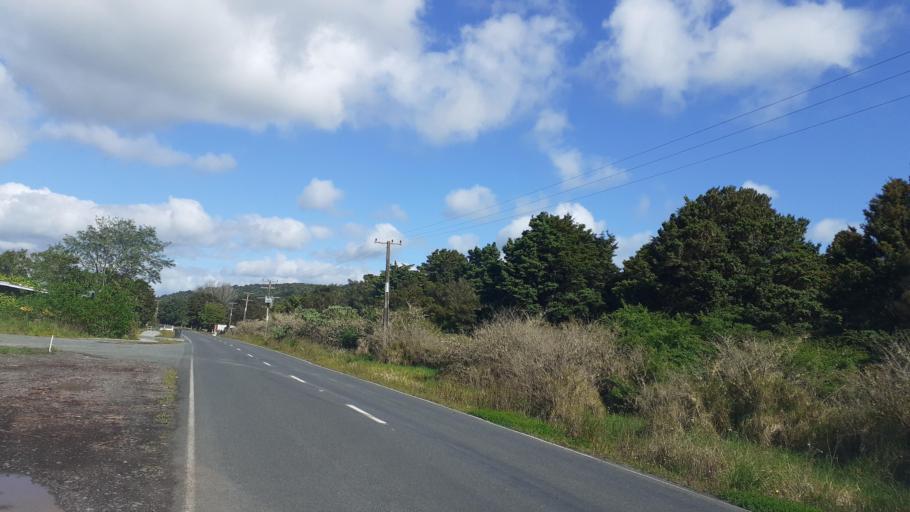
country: NZ
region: Northland
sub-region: Far North District
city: Moerewa
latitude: -35.3983
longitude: 174.0009
